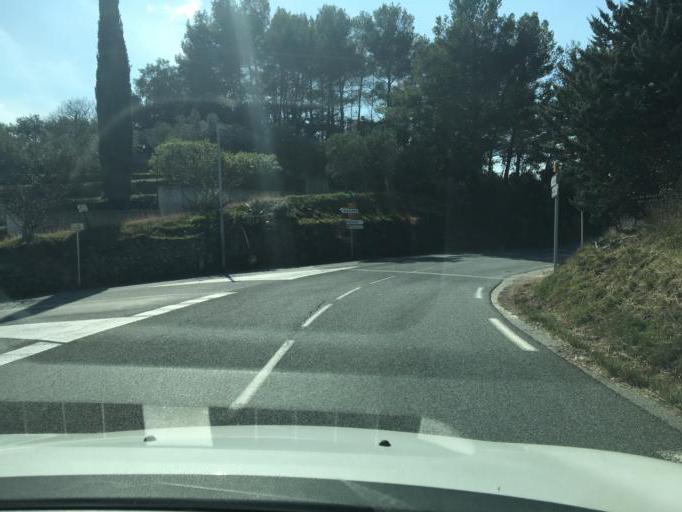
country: FR
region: Provence-Alpes-Cote d'Azur
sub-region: Departement du Var
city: Callas
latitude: 43.5967
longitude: 6.5464
